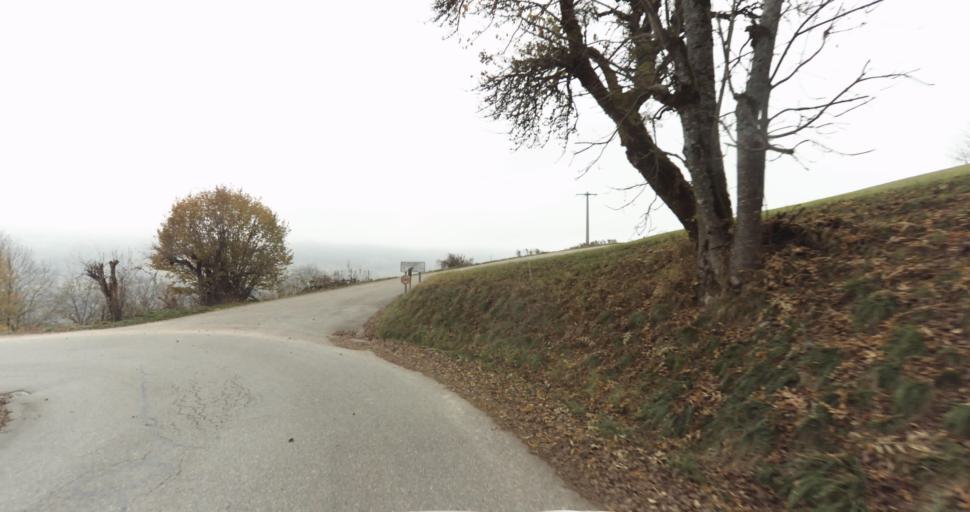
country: FR
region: Rhone-Alpes
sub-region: Departement de la Haute-Savoie
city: Saint-Jorioz
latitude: 45.7798
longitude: 6.1497
